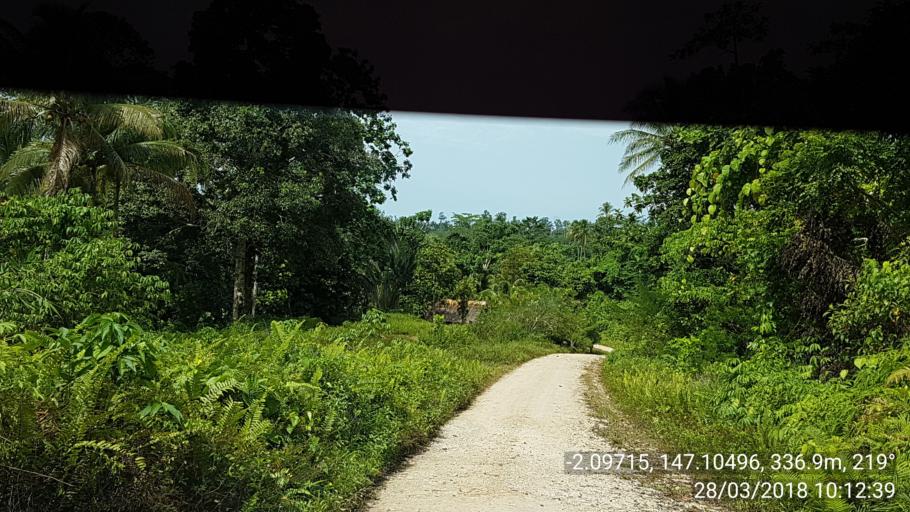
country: PG
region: Manus
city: Lorengau
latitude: -2.0975
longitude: 147.1050
